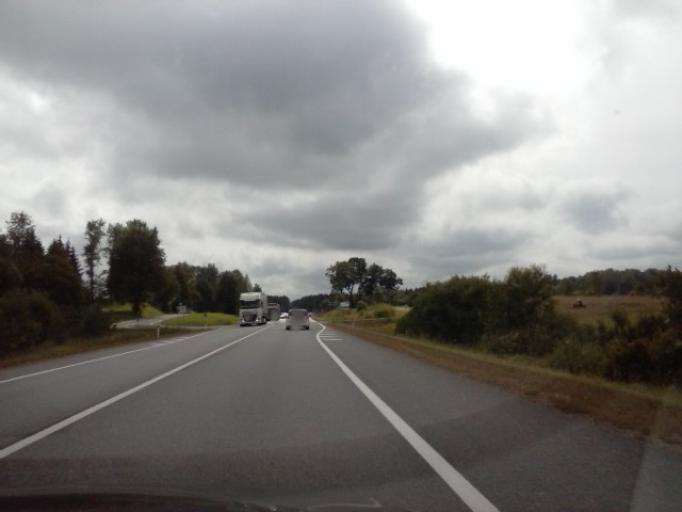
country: LV
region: Kekava
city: Kekava
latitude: 56.7823
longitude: 24.2464
